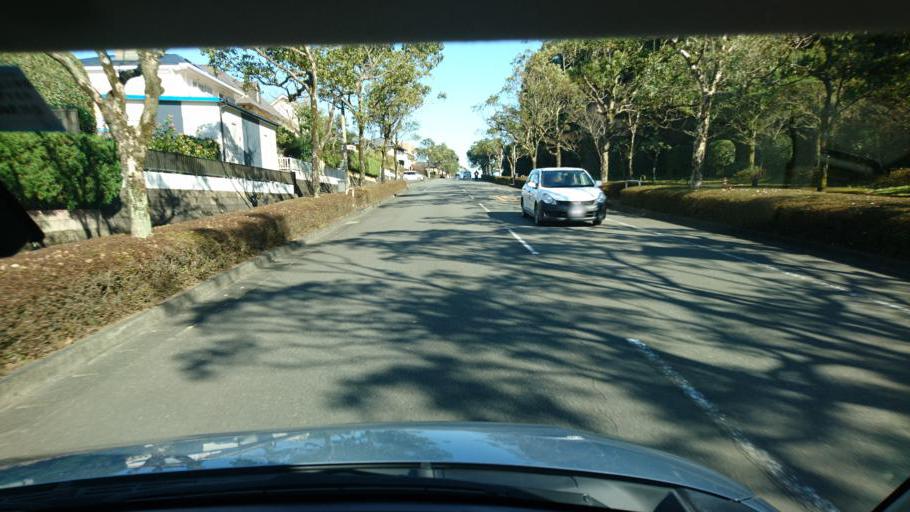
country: JP
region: Miyazaki
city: Miyazaki-shi
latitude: 31.8323
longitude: 131.4294
